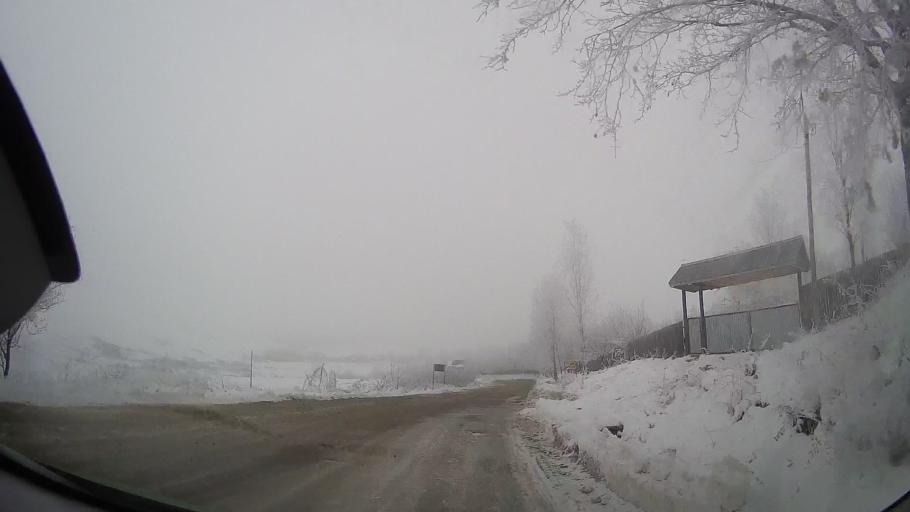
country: RO
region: Neamt
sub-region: Comuna Pancesti
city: Pancesti
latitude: 46.9182
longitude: 27.1665
